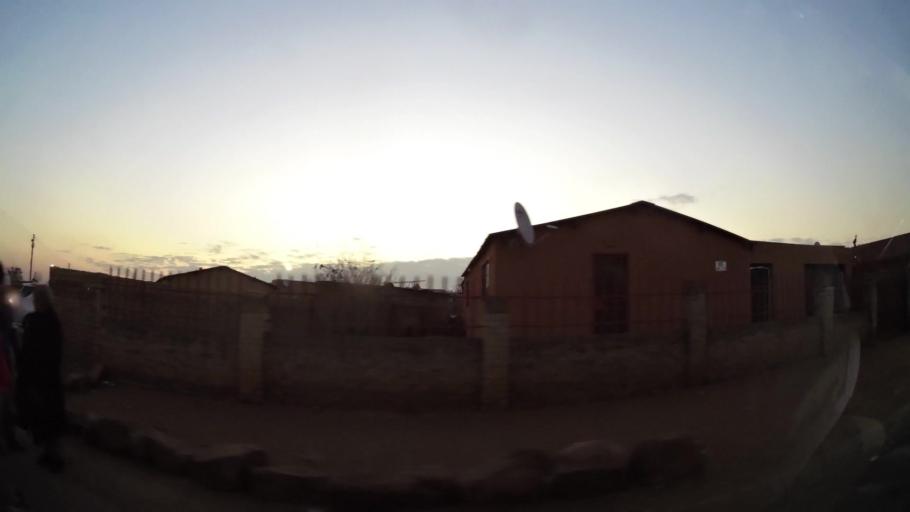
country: ZA
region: Gauteng
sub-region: West Rand District Municipality
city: Randfontein
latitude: -26.2061
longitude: 27.7132
